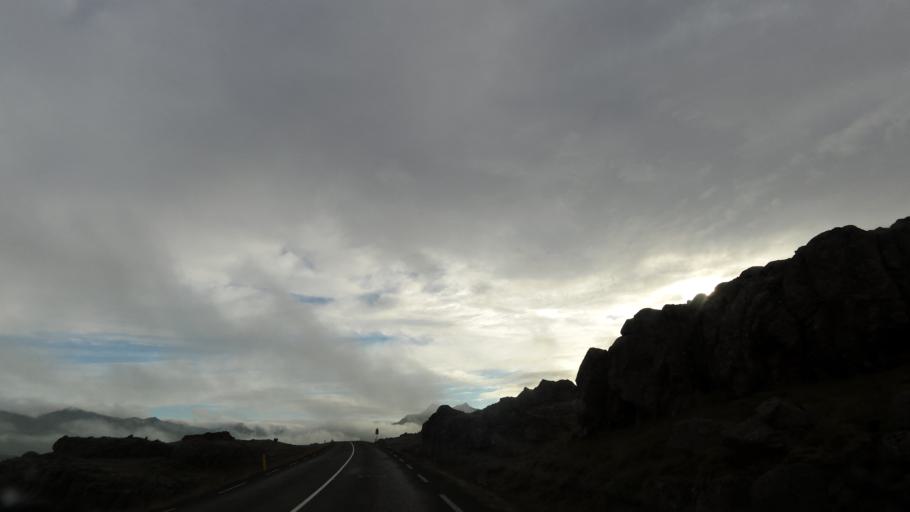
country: IS
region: East
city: Reydarfjoerdur
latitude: 64.5908
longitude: -14.5279
